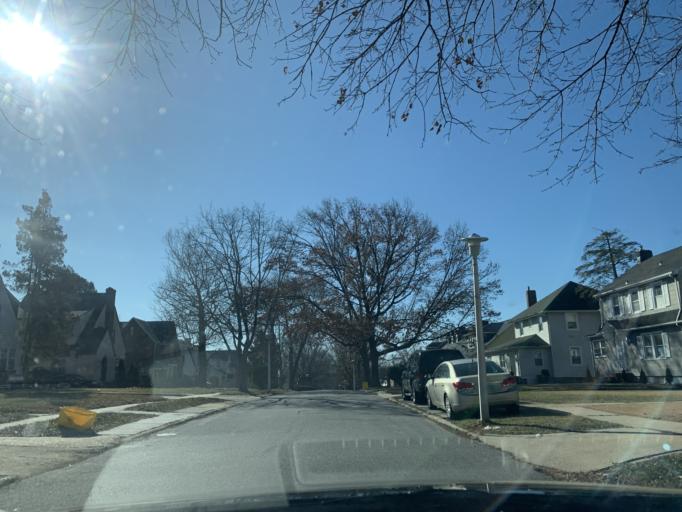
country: US
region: Maryland
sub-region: Baltimore County
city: Lochearn
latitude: 39.3260
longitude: -76.6661
